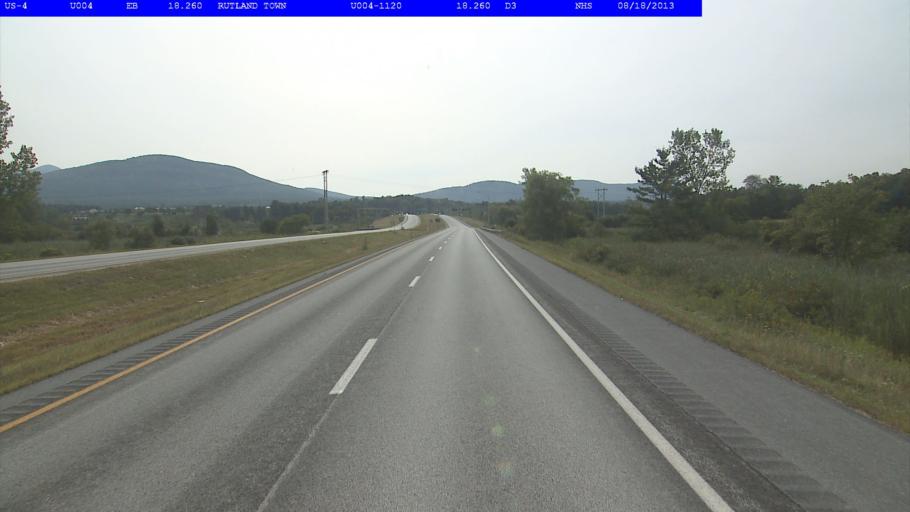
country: US
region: Vermont
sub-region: Rutland County
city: Rutland
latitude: 43.5815
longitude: -72.9772
